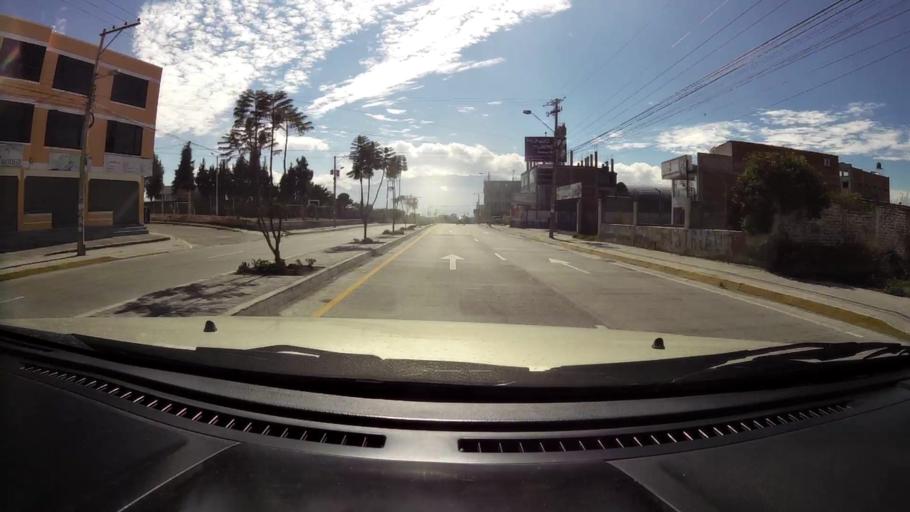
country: EC
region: Chimborazo
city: Riobamba
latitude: -1.6625
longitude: -78.6736
